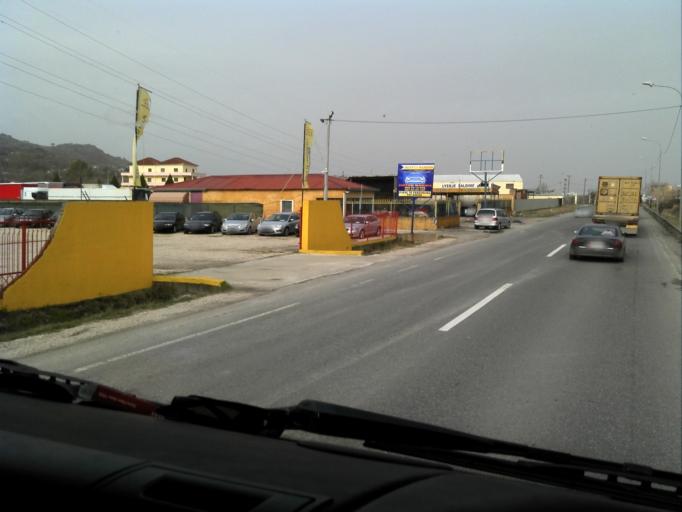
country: AL
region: Tirane
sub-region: Rrethi i Tiranes
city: Preze
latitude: 41.4257
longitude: 19.6877
